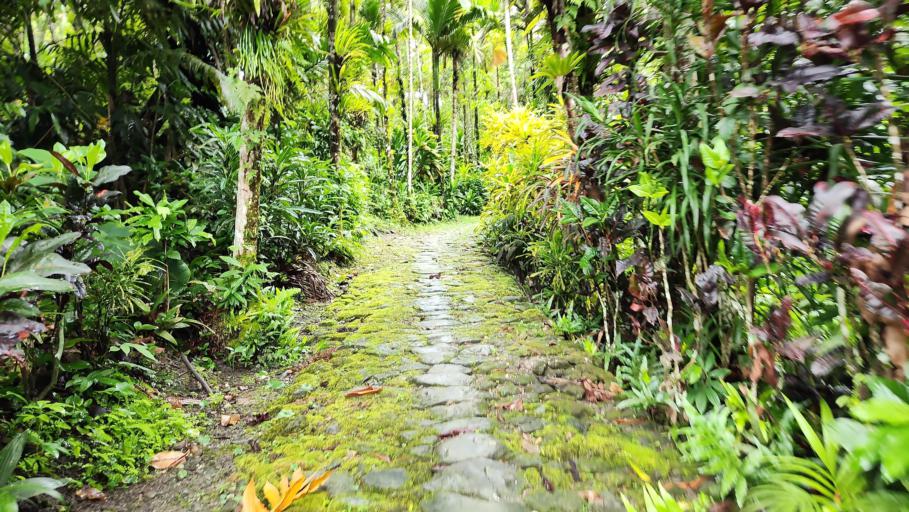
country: FM
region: Yap
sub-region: Weloy Municipality
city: Colonia
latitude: 9.5192
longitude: 138.1186
